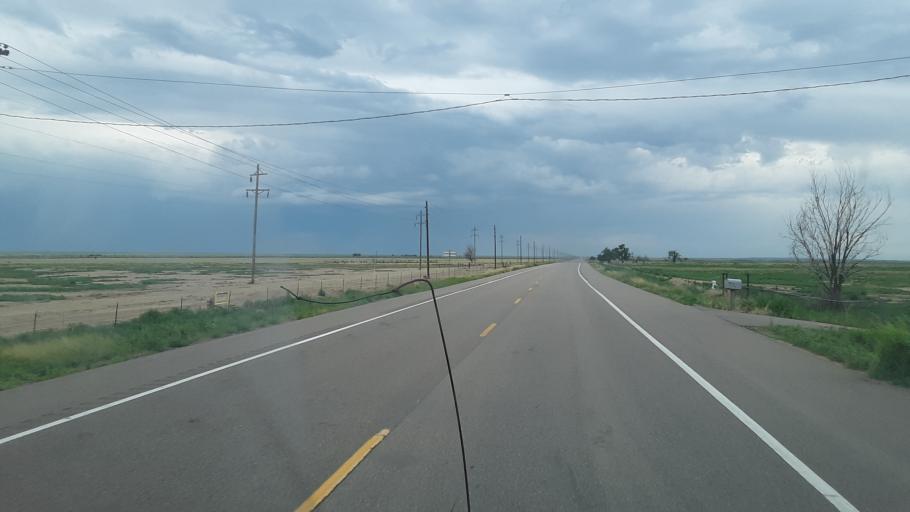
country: US
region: Colorado
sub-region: Crowley County
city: Ordway
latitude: 38.1989
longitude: -103.7482
